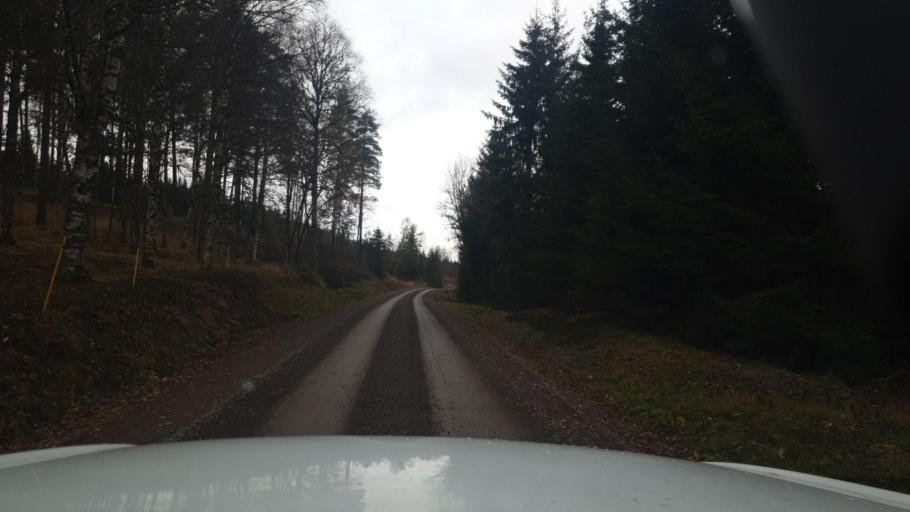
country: SE
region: Vaermland
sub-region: Eda Kommun
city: Charlottenberg
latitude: 60.0760
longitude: 12.5264
